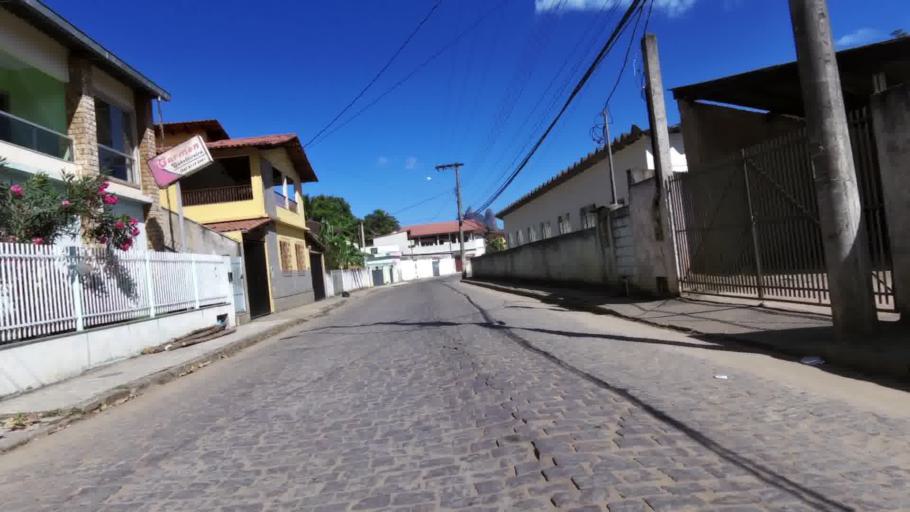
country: BR
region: Espirito Santo
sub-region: Rio Novo Do Sul
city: Rio Novo do Sul
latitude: -20.8651
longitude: -40.9351
